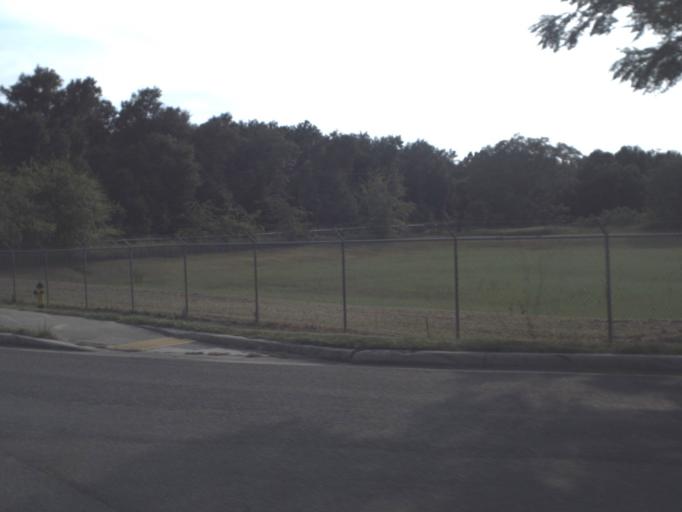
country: US
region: Florida
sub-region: Hernando County
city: Masaryktown
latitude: 28.4561
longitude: -82.4497
